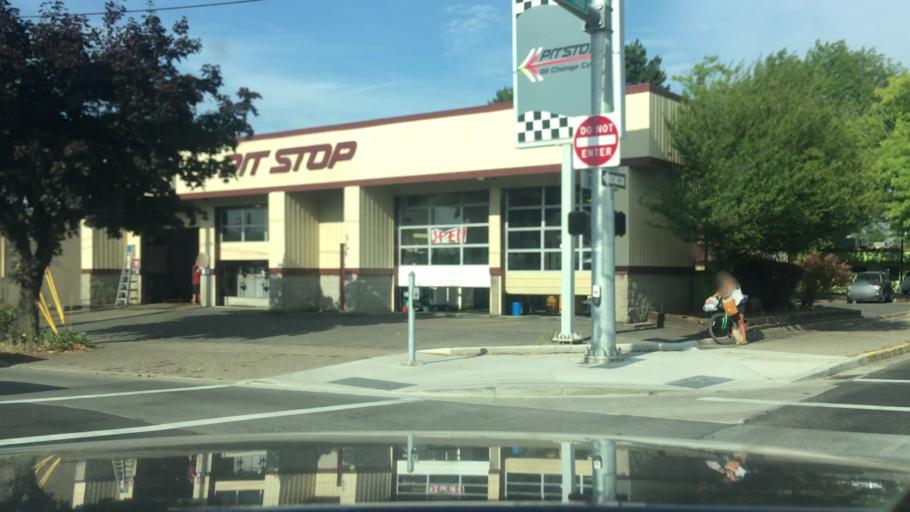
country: US
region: Oregon
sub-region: Lane County
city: Eugene
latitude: 44.0478
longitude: -123.1230
